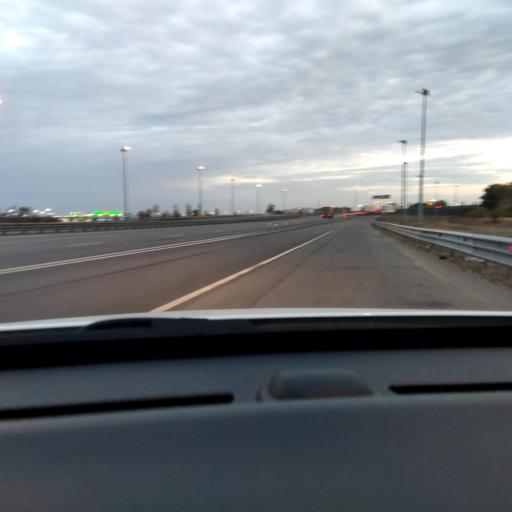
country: RU
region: Voronezj
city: Somovo
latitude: 51.6564
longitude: 39.3025
